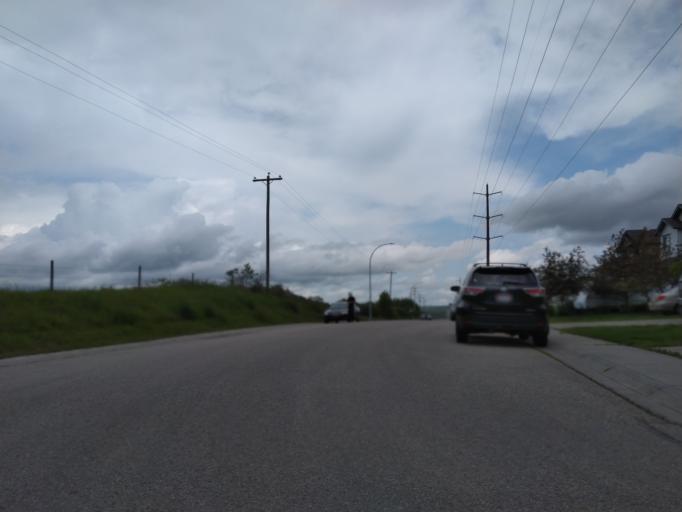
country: CA
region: Alberta
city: Cochrane
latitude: 51.1837
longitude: -114.5132
